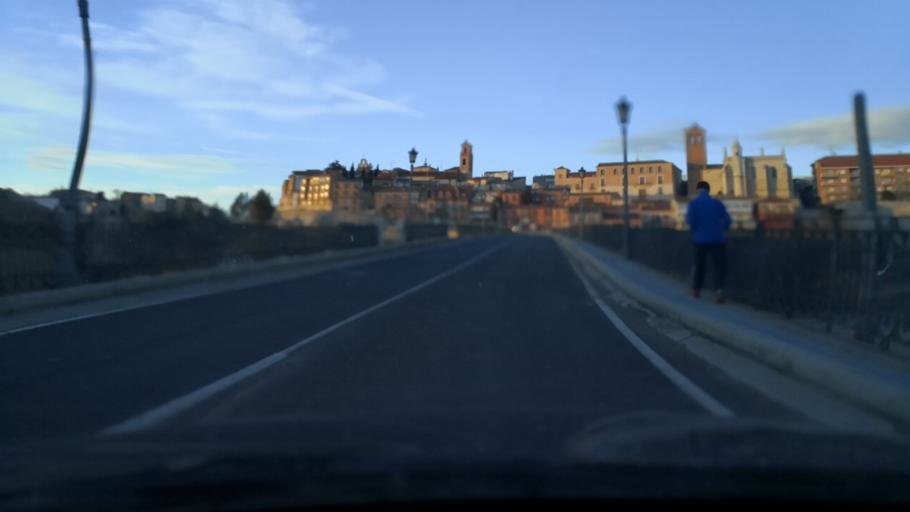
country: ES
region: Castille and Leon
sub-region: Provincia de Valladolid
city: Tordesillas
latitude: 41.4974
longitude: -5.0007
